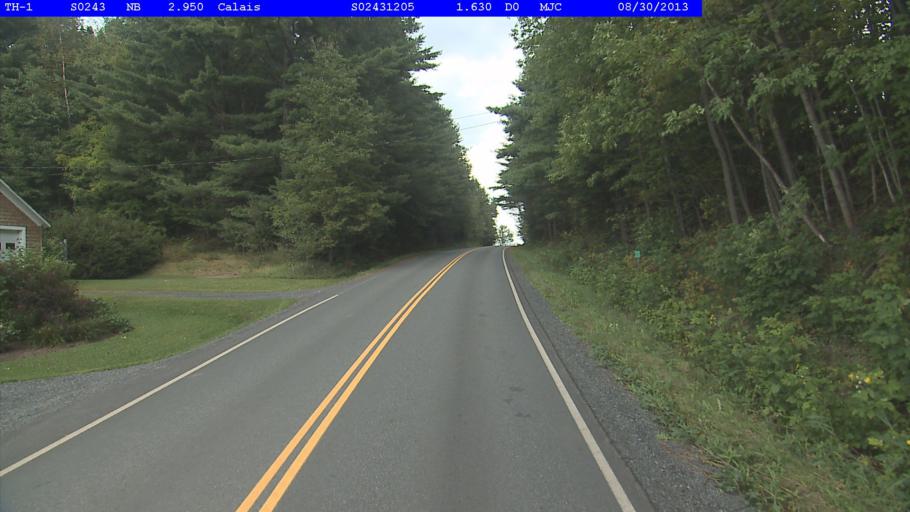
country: US
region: Vermont
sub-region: Washington County
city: Montpelier
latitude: 44.3564
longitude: -72.5106
